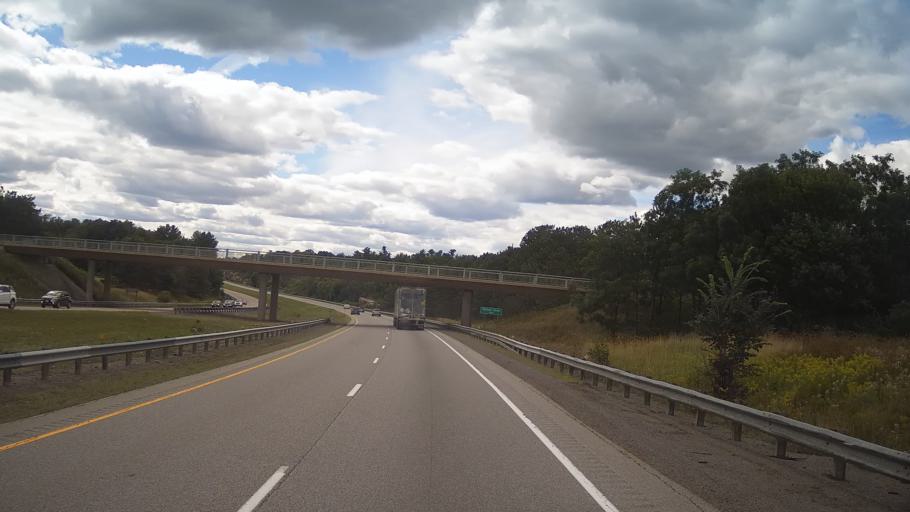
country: CA
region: Ontario
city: Brockville
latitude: 44.5205
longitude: -75.8020
